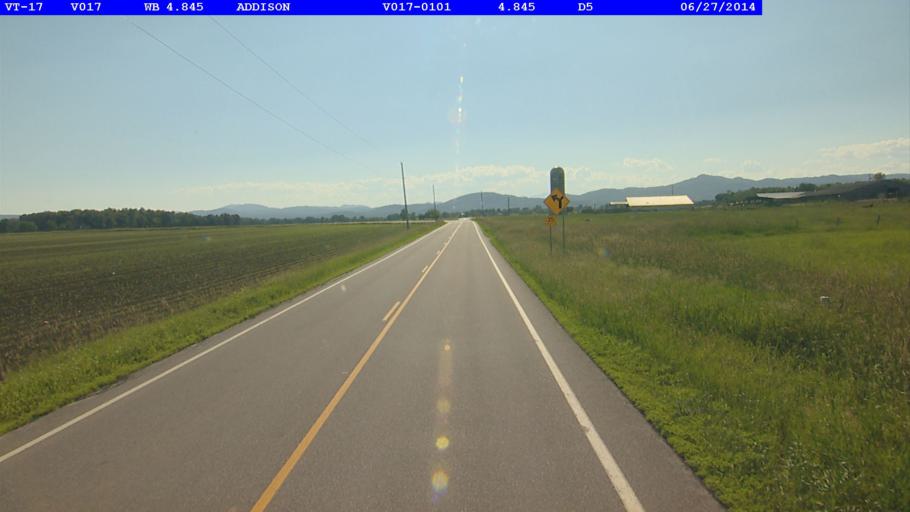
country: US
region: New York
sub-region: Essex County
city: Port Henry
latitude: 44.0814
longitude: -73.3721
